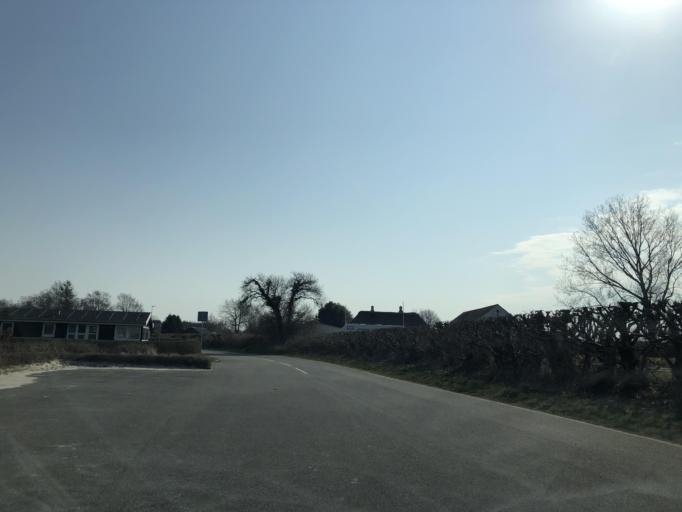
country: DK
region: South Denmark
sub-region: Sonderborg Kommune
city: Nordborg
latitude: 55.0796
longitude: 9.7283
